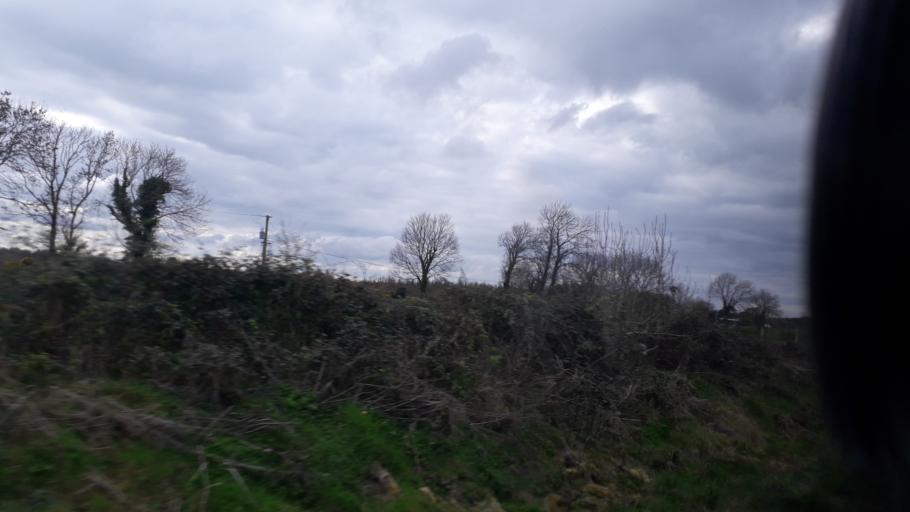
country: IE
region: Leinster
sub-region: An Iarmhi
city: Castlepollard
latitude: 53.6489
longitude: -7.4274
